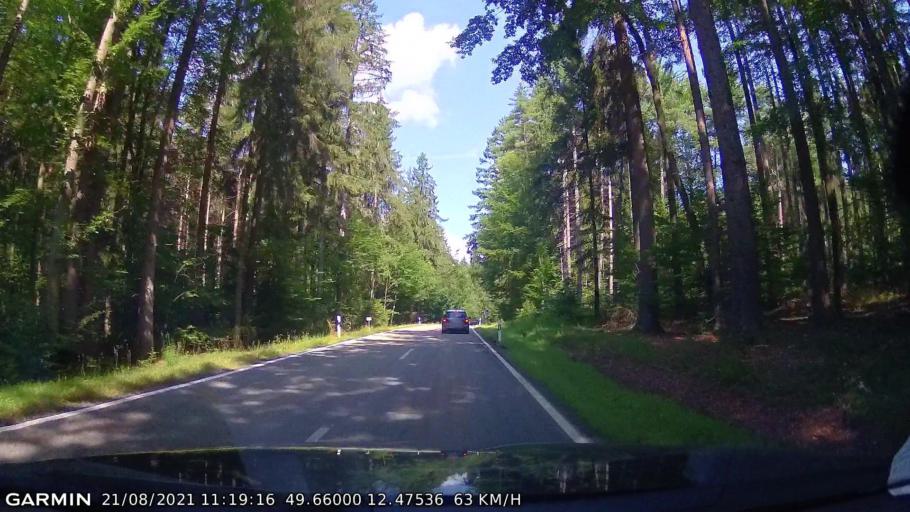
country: DE
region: Bavaria
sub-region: Upper Palatinate
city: Waidhaus
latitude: 49.6600
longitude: 12.4753
